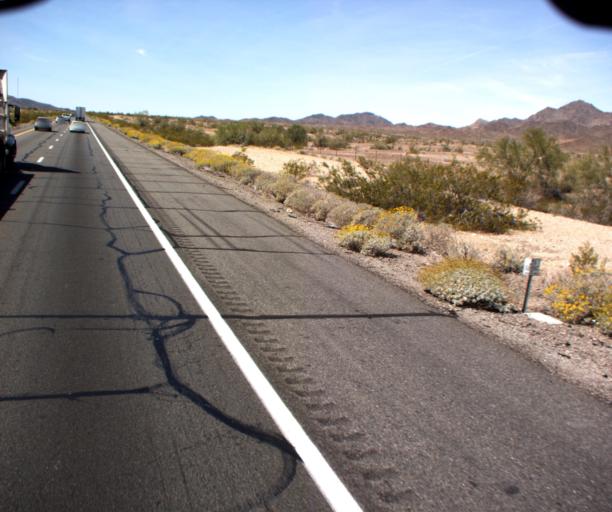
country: US
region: Arizona
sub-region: La Paz County
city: Quartzsite
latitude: 33.6522
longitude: -114.2952
